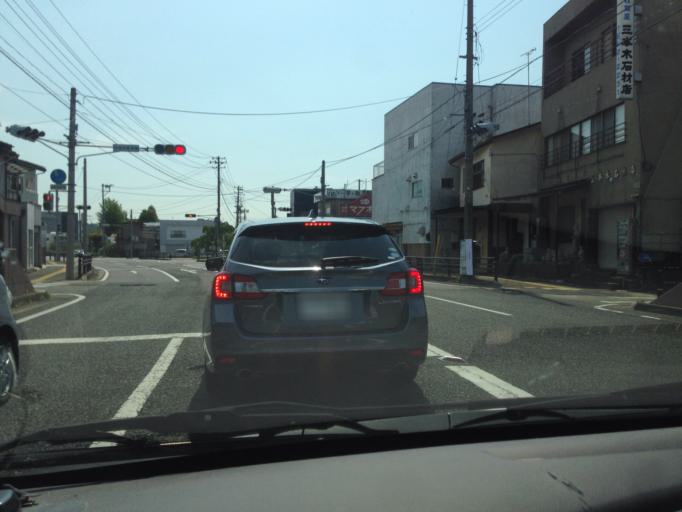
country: JP
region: Tochigi
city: Kuroiso
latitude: 37.1297
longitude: 140.2039
